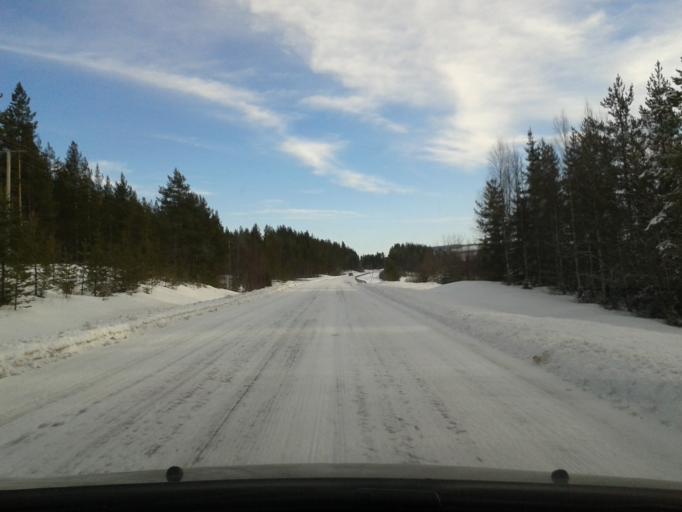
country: SE
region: Vaesterbotten
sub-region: Asele Kommun
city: Asele
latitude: 64.3491
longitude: 16.9937
